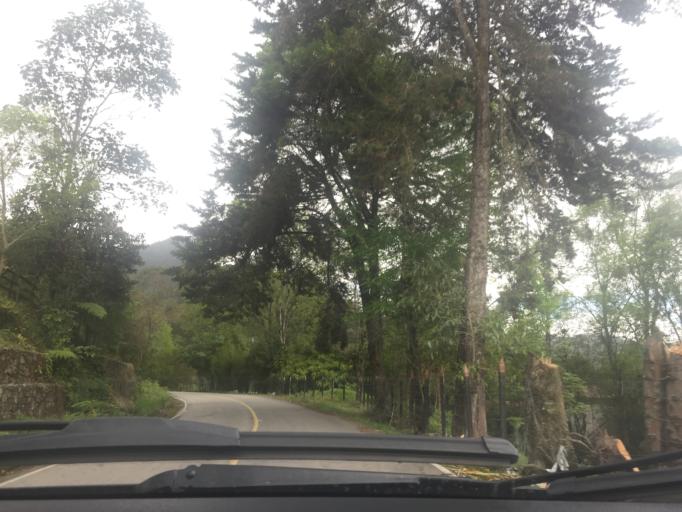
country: CO
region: Cundinamarca
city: Supata
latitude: 5.0438
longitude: -74.2420
